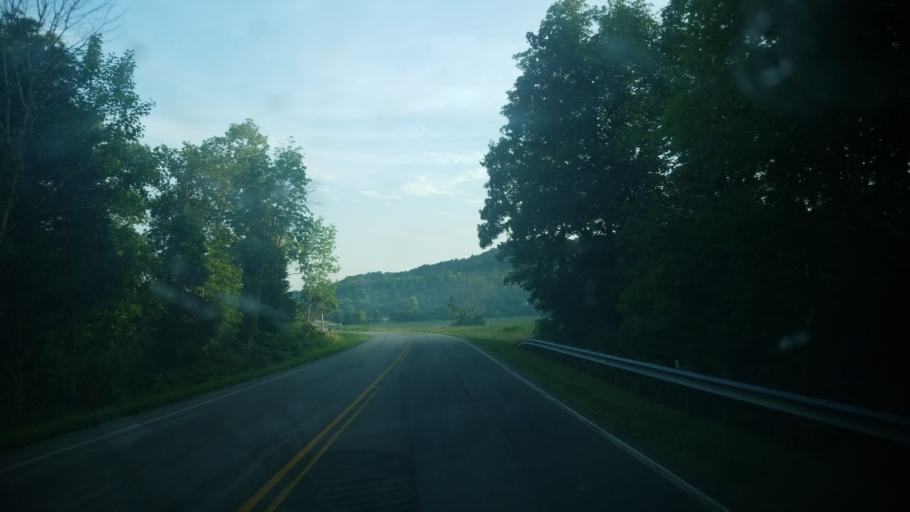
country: US
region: Ohio
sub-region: Adams County
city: Peebles
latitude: 38.8869
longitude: -83.4555
